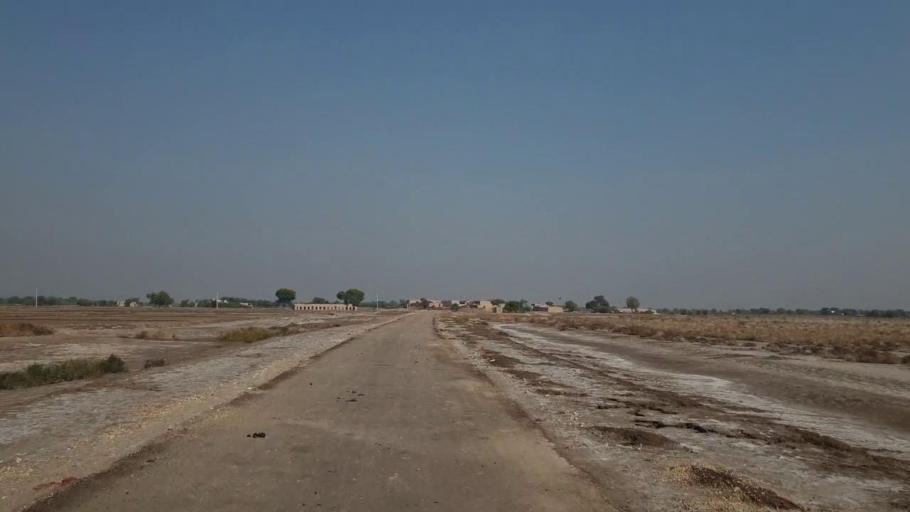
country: PK
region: Sindh
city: Sehwan
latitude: 26.4304
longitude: 67.7716
